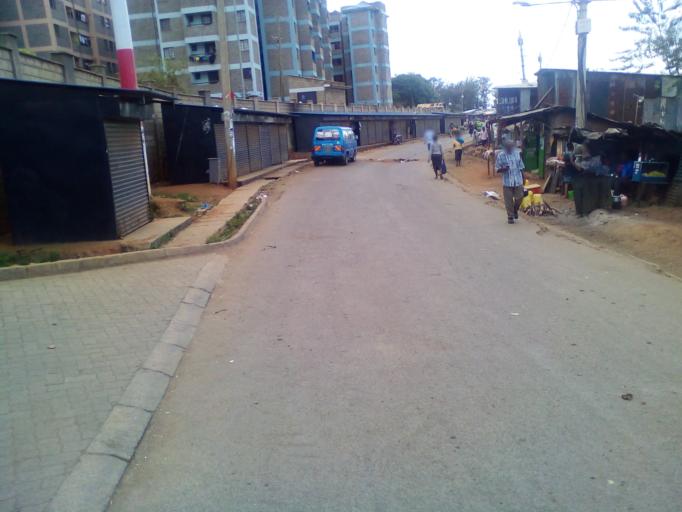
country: KE
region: Nairobi Area
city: Nairobi
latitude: -1.3149
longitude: 36.8009
